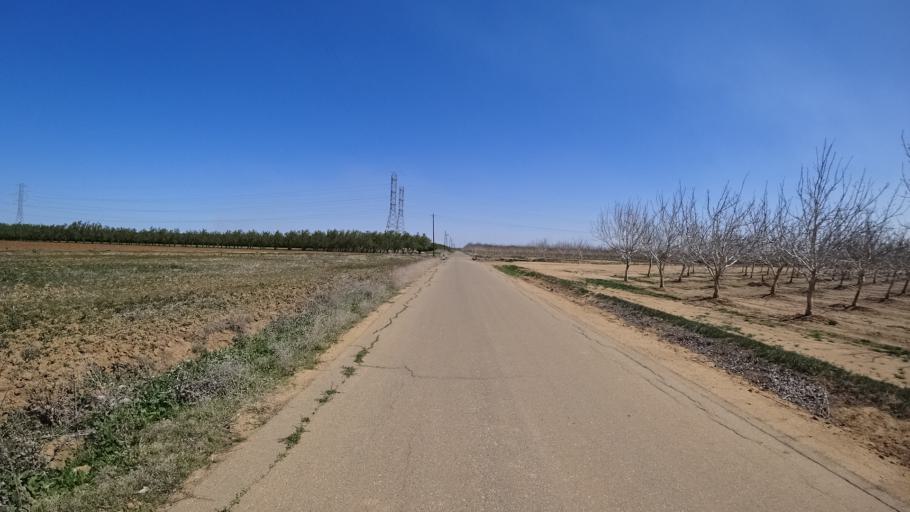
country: US
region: California
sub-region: Glenn County
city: Willows
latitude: 39.4510
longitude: -122.2654
